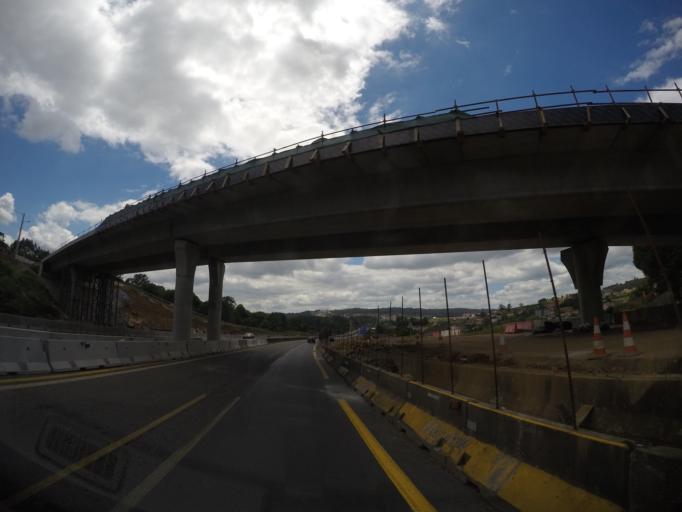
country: ES
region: Galicia
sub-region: Provincia da Coruna
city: Rois
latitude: 42.8199
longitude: -8.7531
